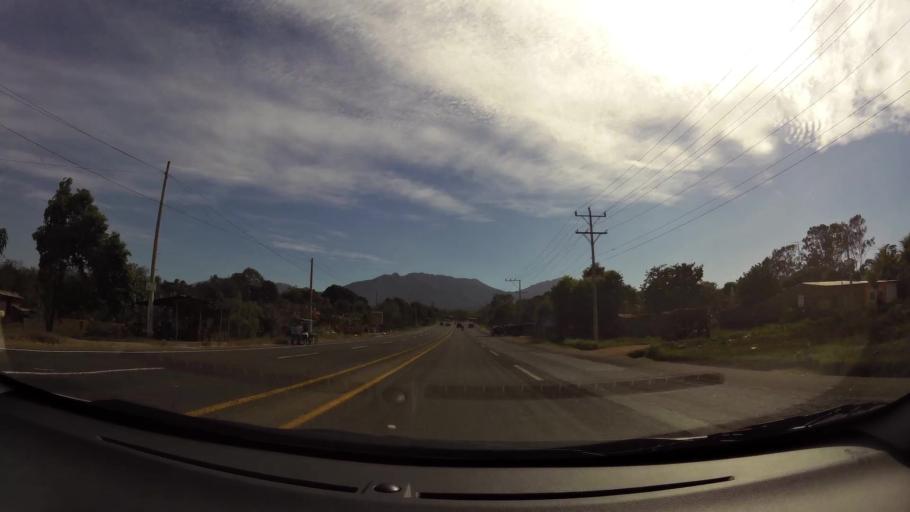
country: SV
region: Santa Ana
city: Chalchuapa
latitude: 13.9807
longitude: -89.6904
